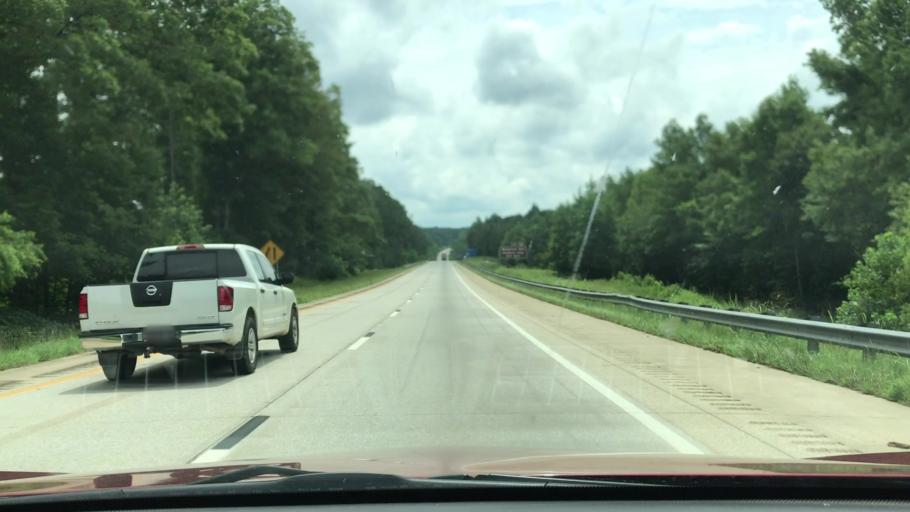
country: US
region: South Carolina
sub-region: Laurens County
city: Clinton
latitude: 34.5157
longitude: -81.8818
